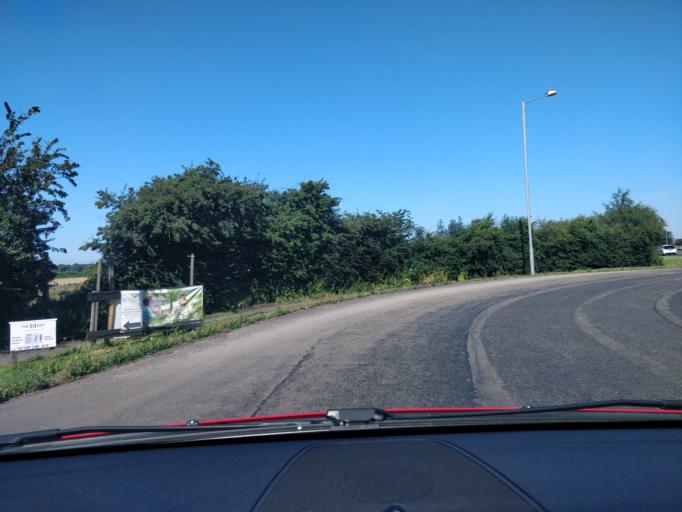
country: GB
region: England
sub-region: Lancashire
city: Banks
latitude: 53.6728
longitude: -2.9222
